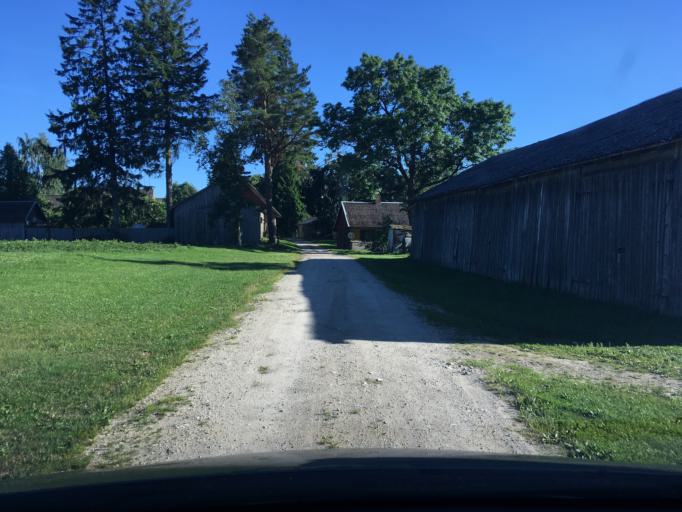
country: EE
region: Laeaene
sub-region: Lihula vald
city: Lihula
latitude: 58.5833
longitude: 23.7364
